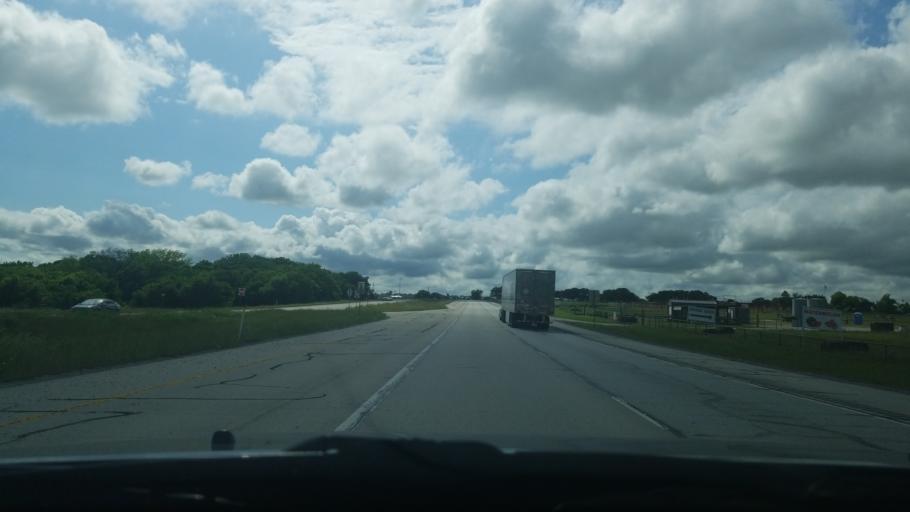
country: US
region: Texas
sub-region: Denton County
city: Ponder
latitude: 33.2499
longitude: -97.4059
